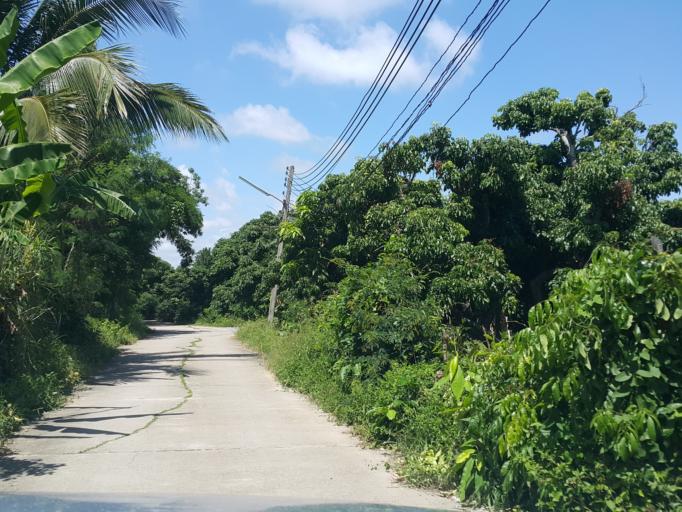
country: TH
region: Chiang Mai
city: San Kamphaeng
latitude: 18.6954
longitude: 99.1156
